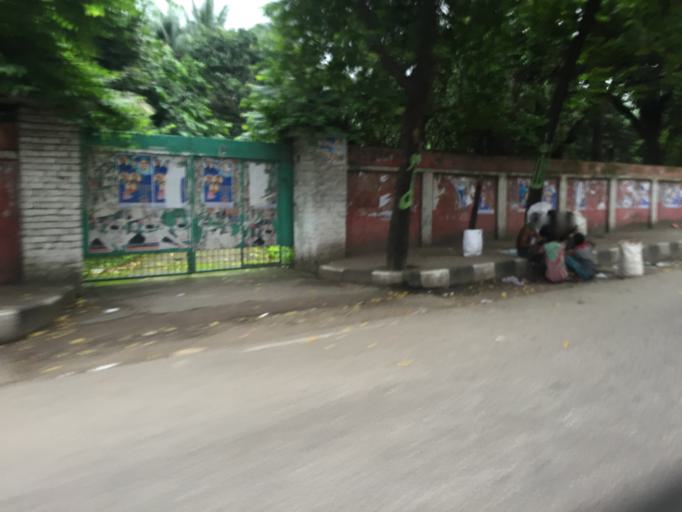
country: BD
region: Dhaka
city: Paltan
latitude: 23.7250
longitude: 90.4047
